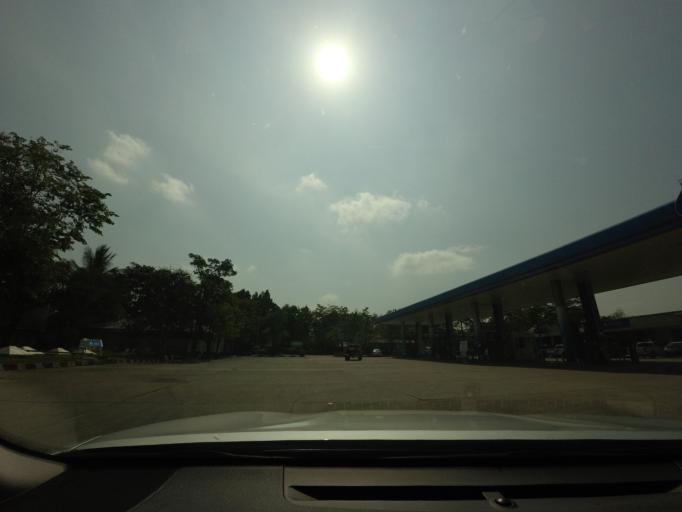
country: TH
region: Prachuap Khiri Khan
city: Hua Hin
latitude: 12.6840
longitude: 99.8934
